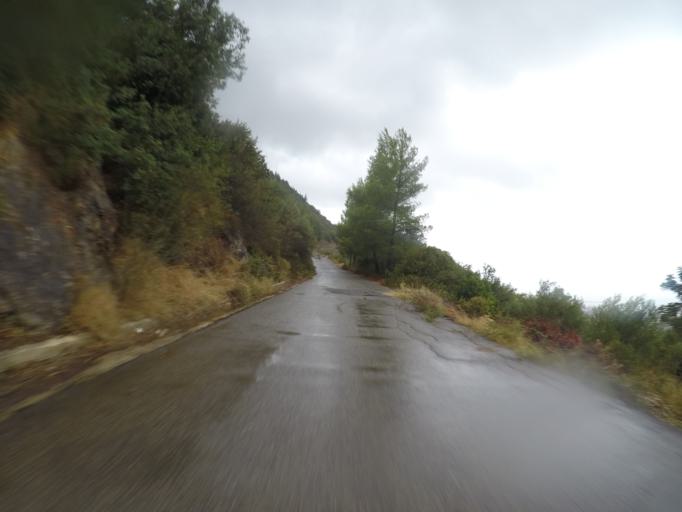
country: GR
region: Peloponnese
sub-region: Nomos Messinias
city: Kyparissia
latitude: 37.2508
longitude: 21.6852
